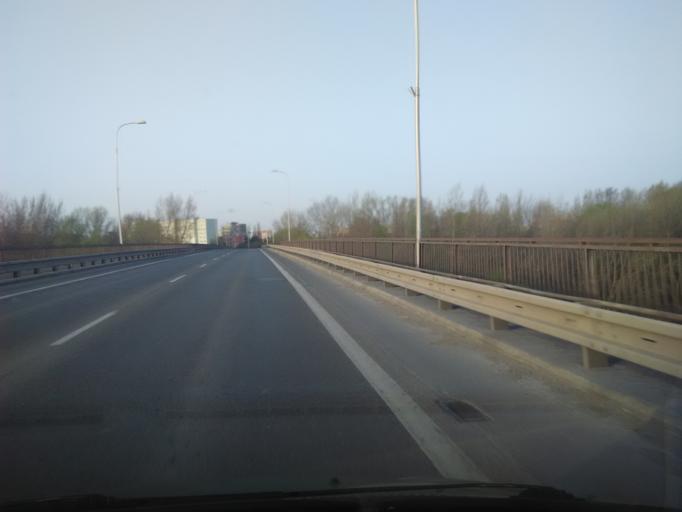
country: SK
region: Nitriansky
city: Sellye
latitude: 48.1607
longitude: 17.8804
